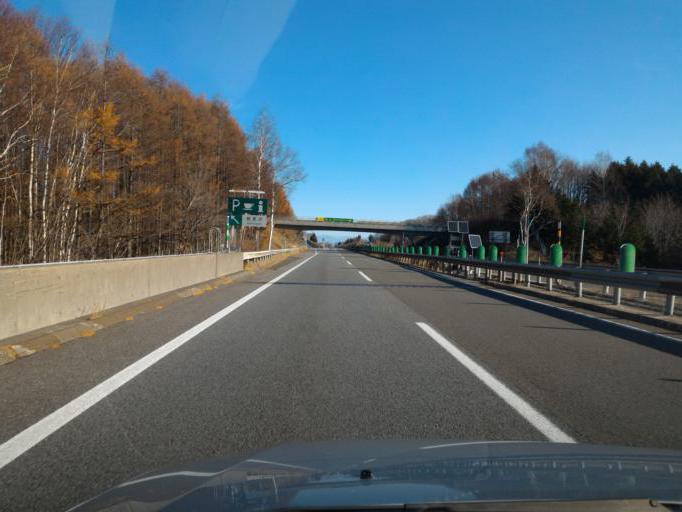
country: JP
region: Hokkaido
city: Iwamizawa
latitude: 43.1903
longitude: 141.7946
